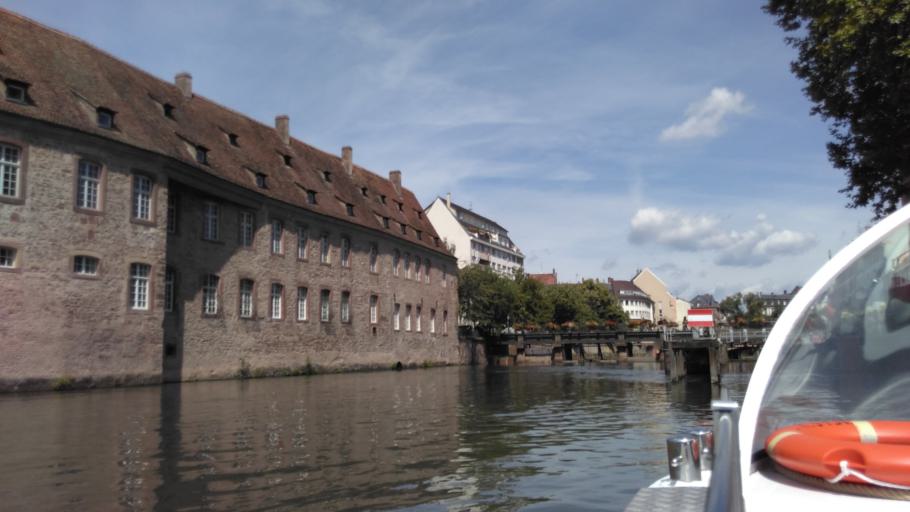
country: FR
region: Alsace
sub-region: Departement du Bas-Rhin
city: Strasbourg
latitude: 48.5806
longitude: 7.7384
